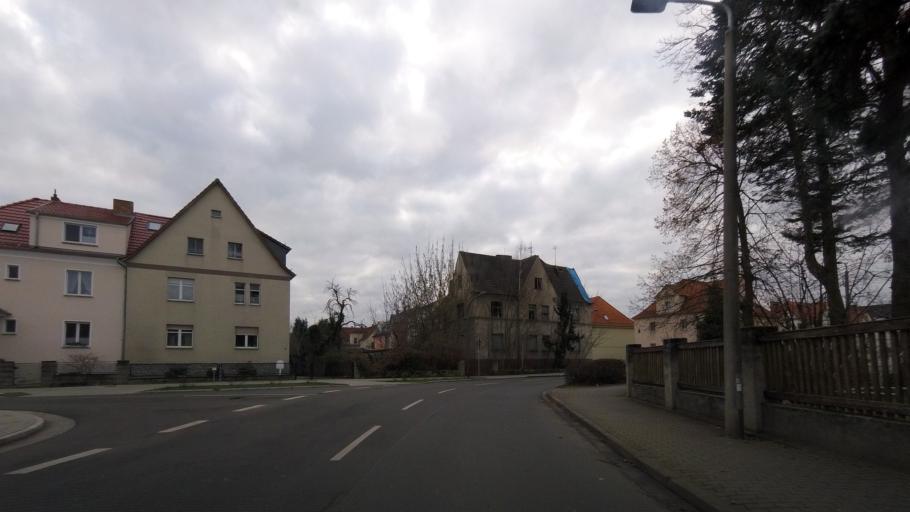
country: DE
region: Brandenburg
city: Juterbog
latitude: 51.9947
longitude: 13.0790
